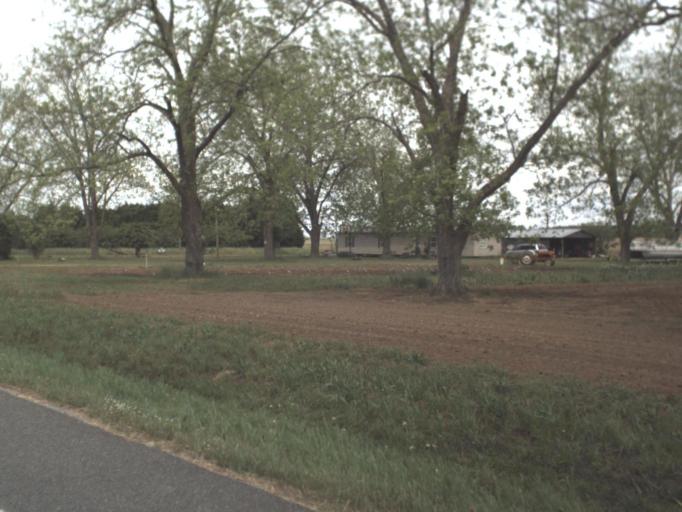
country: US
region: Florida
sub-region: Santa Rosa County
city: Point Baker
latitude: 30.7891
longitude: -87.0924
